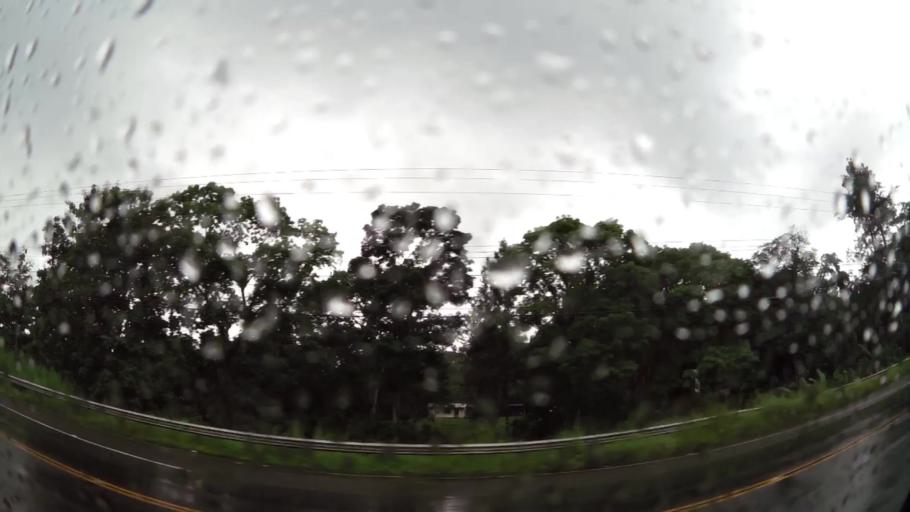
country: PA
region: Colon
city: Buena Vista
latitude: 9.2769
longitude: -79.7008
